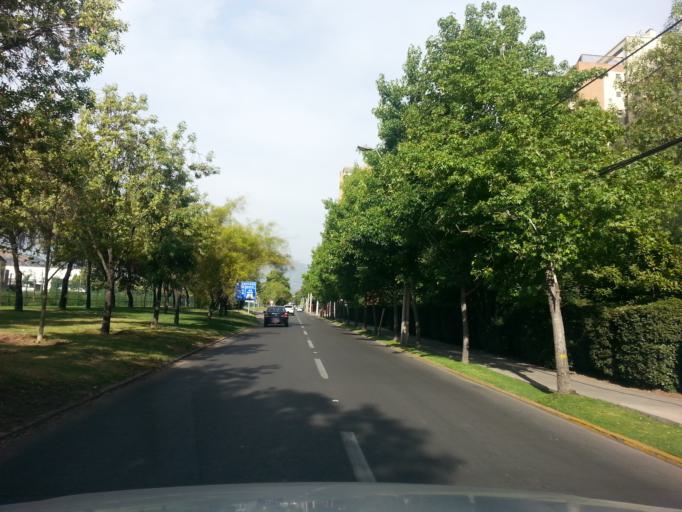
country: CL
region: Santiago Metropolitan
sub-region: Provincia de Santiago
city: Villa Presidente Frei, Nunoa, Santiago, Chile
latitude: -33.3944
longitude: -70.5601
